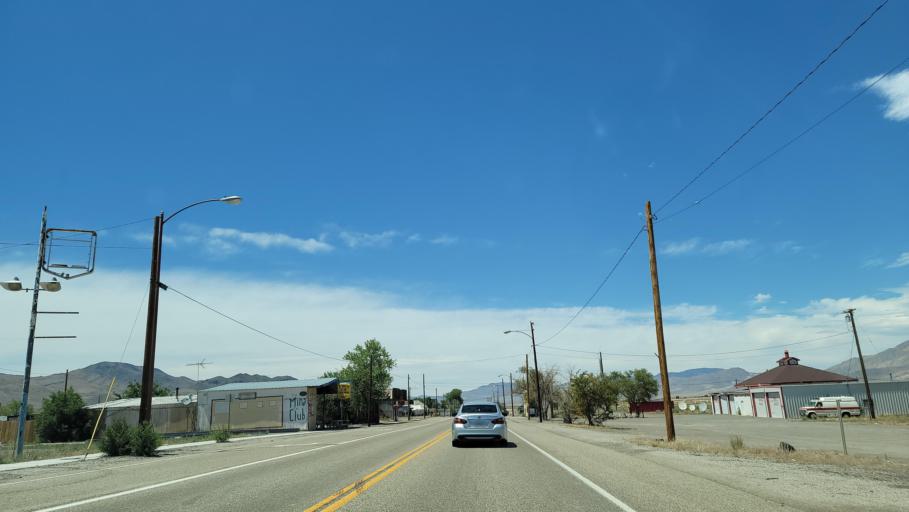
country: US
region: Nevada
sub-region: Mineral County
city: Hawthorne
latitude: 38.3899
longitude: -118.1082
